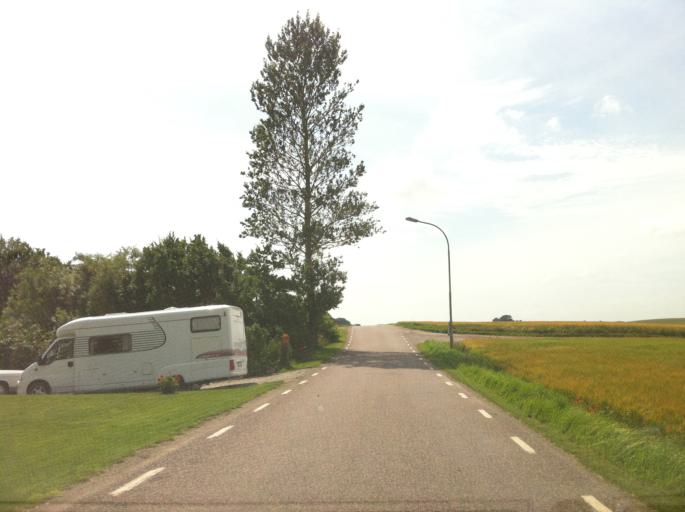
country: SE
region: Skane
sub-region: Skurups Kommun
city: Skurup
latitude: 55.4411
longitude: 13.4432
